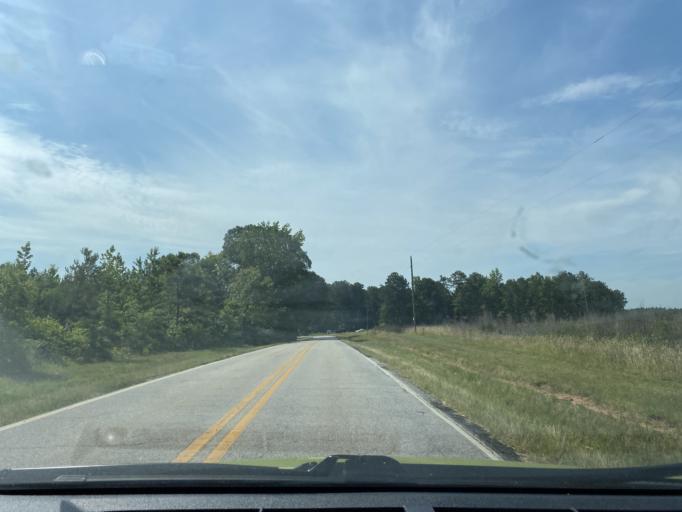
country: US
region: Georgia
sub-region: Coweta County
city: Grantville
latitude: 33.1784
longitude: -84.6985
